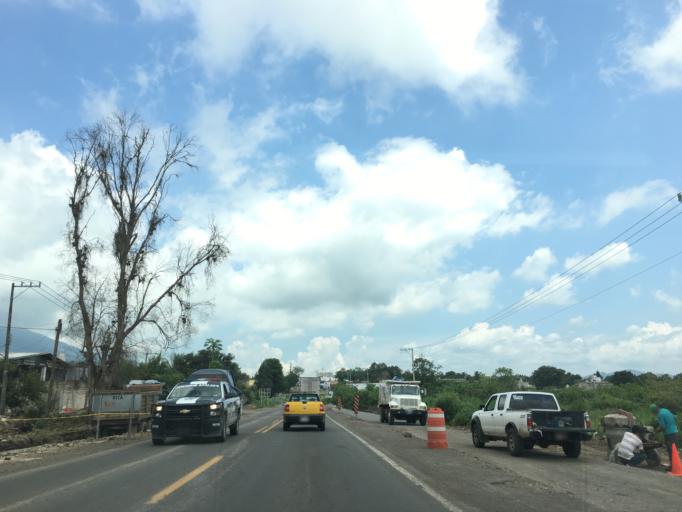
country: MX
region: Nayarit
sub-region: Tepic
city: La Corregidora
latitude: 21.4544
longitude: -104.8209
